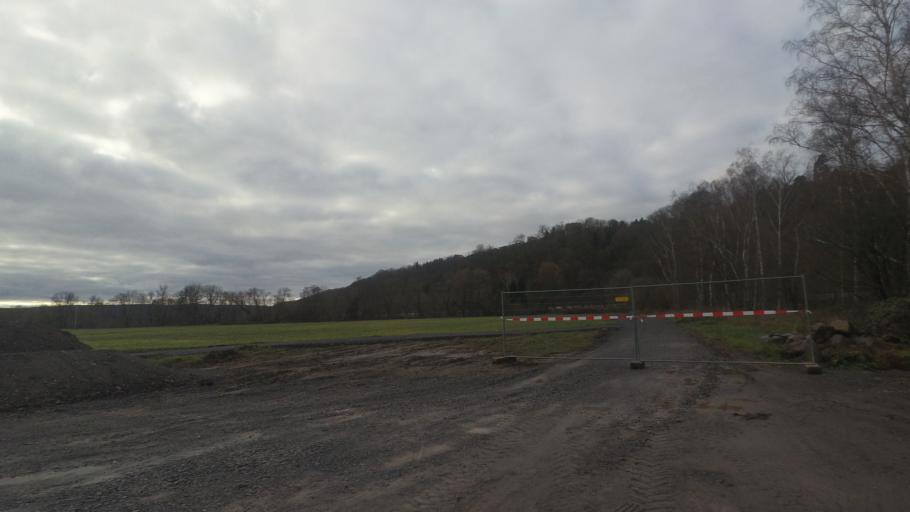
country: DE
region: Thuringia
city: Orlamunde
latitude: 50.7722
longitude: 11.5217
